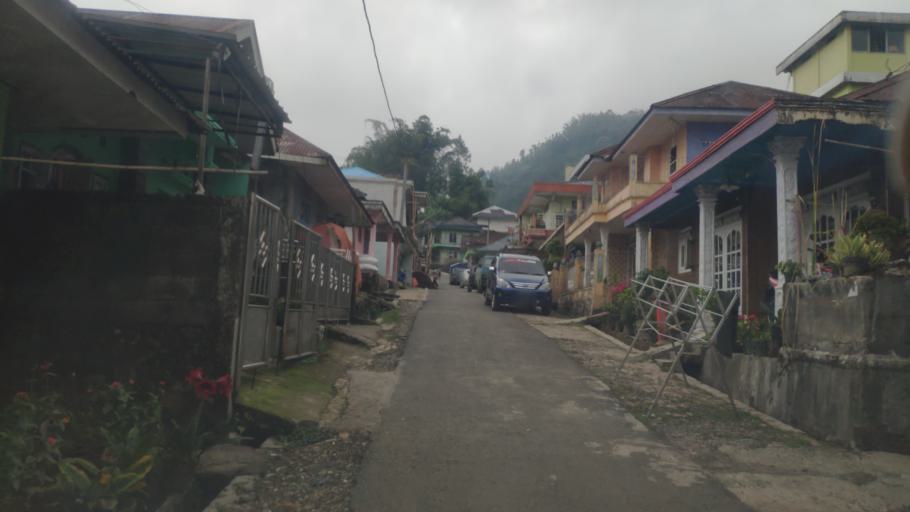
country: ID
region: Central Java
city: Wonosobo
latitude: -7.2300
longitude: 109.7175
